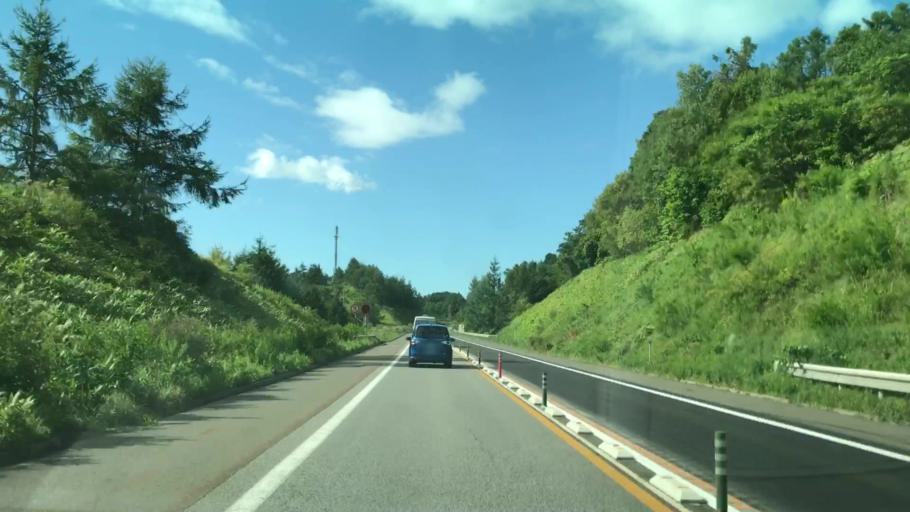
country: JP
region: Hokkaido
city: Date
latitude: 42.4397
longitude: 140.9186
